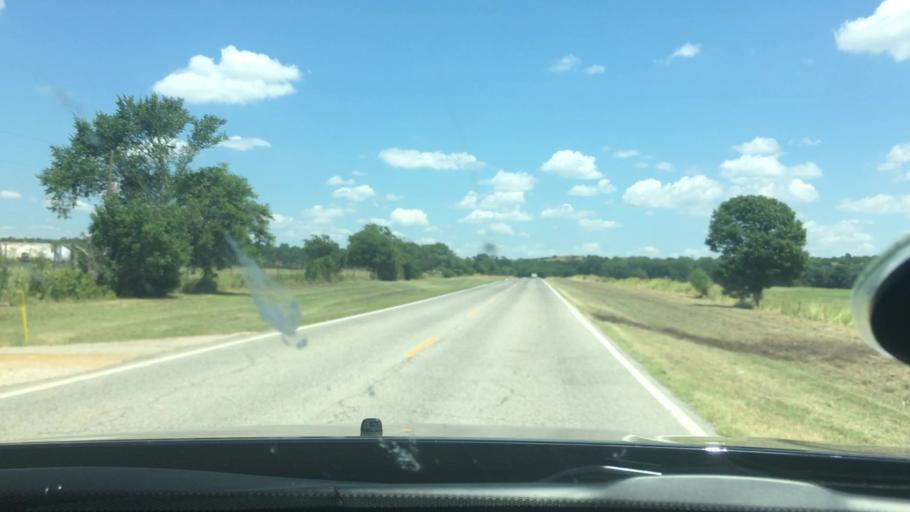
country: US
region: Oklahoma
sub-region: Carter County
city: Dickson
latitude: 34.2978
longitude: -96.9661
